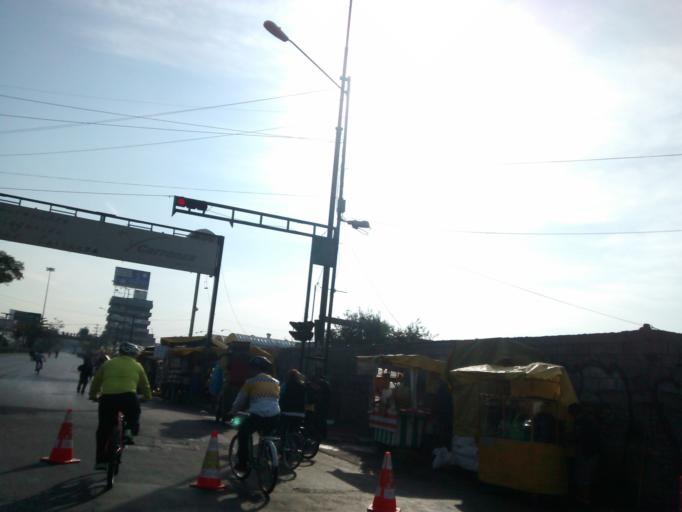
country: MX
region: Mexico City
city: Mexico City
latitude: 19.4228
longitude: -99.1261
